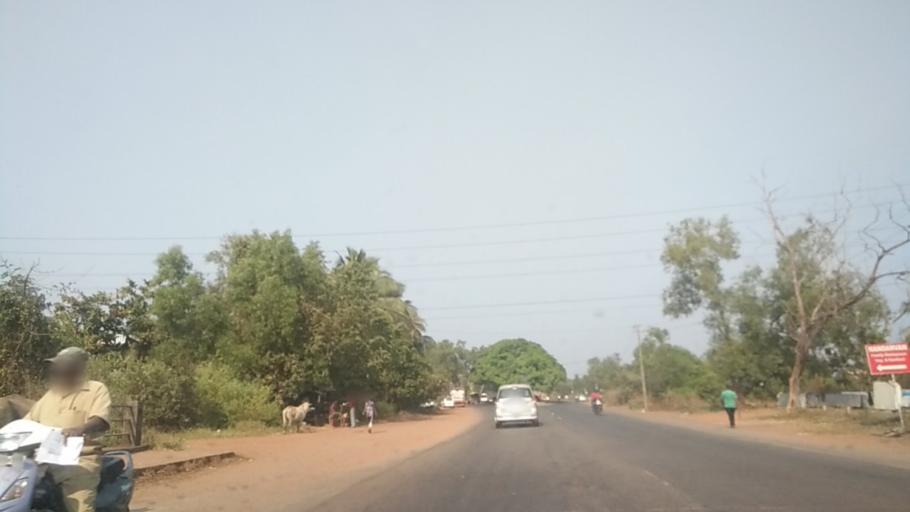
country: IN
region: Goa
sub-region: North Goa
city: Colovale
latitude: 15.6319
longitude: 73.8280
